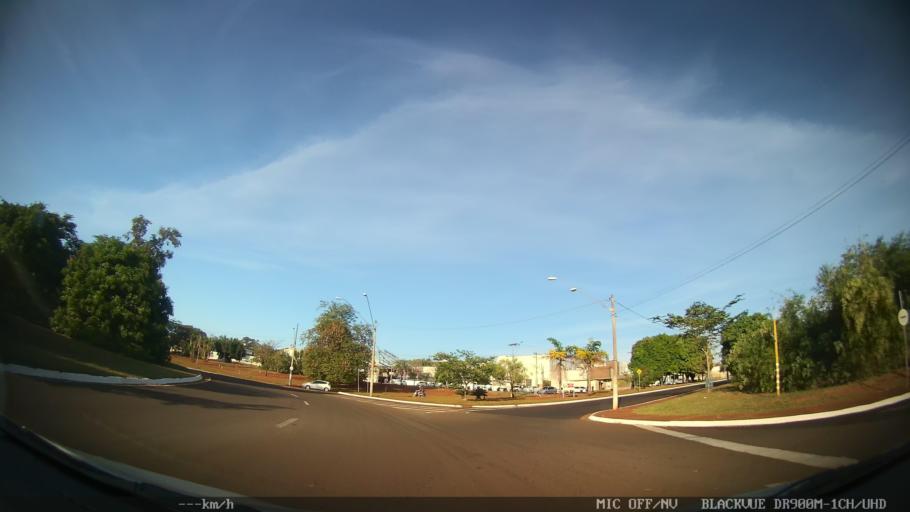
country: BR
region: Sao Paulo
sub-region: Ribeirao Preto
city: Ribeirao Preto
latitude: -21.2153
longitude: -47.7814
